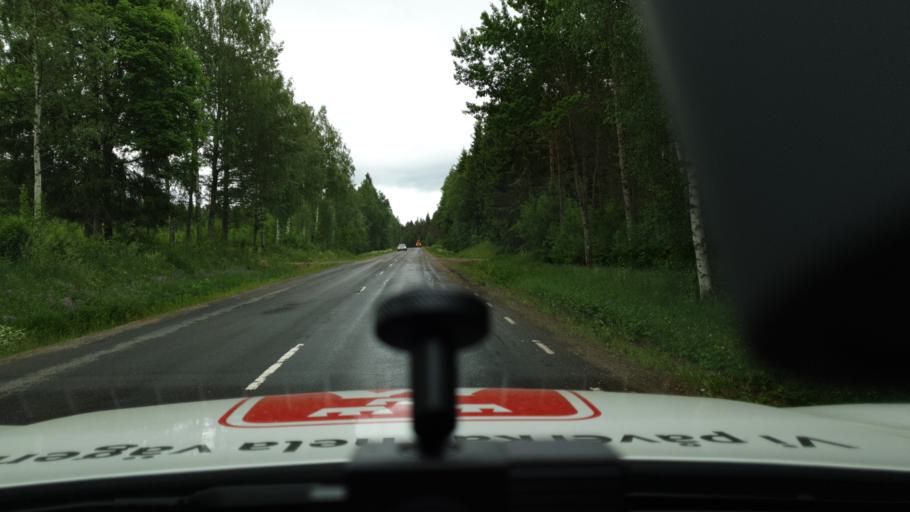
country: SE
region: Joenkoeping
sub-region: Mullsjo Kommun
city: Mullsjoe
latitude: 57.9846
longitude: 13.8009
